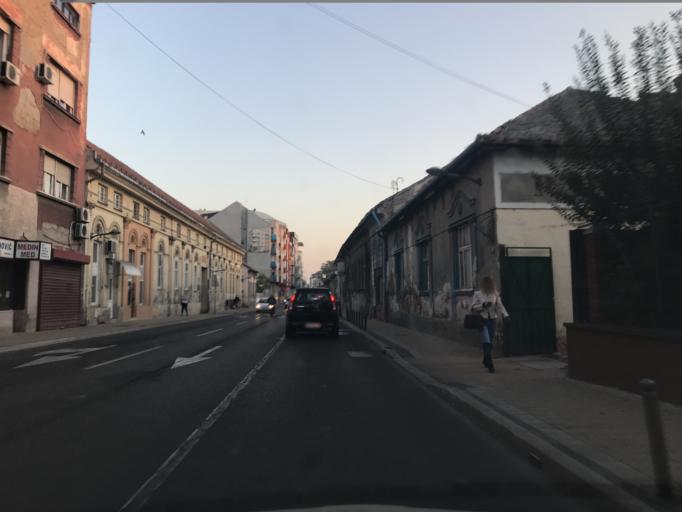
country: RS
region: Autonomna Pokrajina Vojvodina
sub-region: Juznobacki Okrug
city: Novi Sad
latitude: 45.2583
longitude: 19.8422
